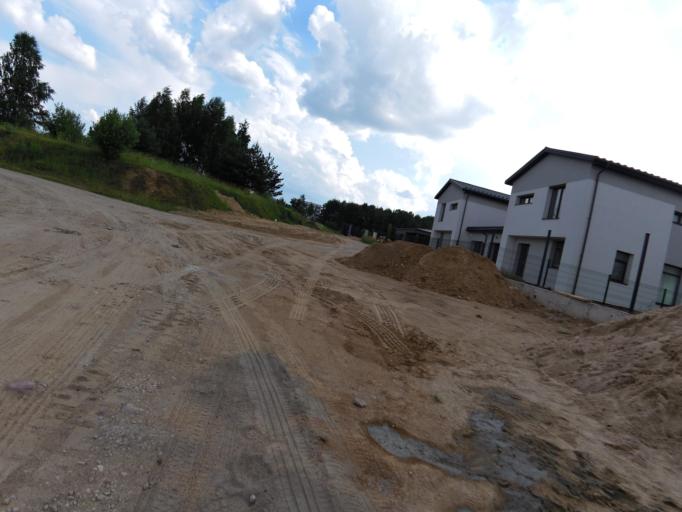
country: LT
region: Vilnius County
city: Pasilaiciai
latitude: 54.7539
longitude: 25.2258
